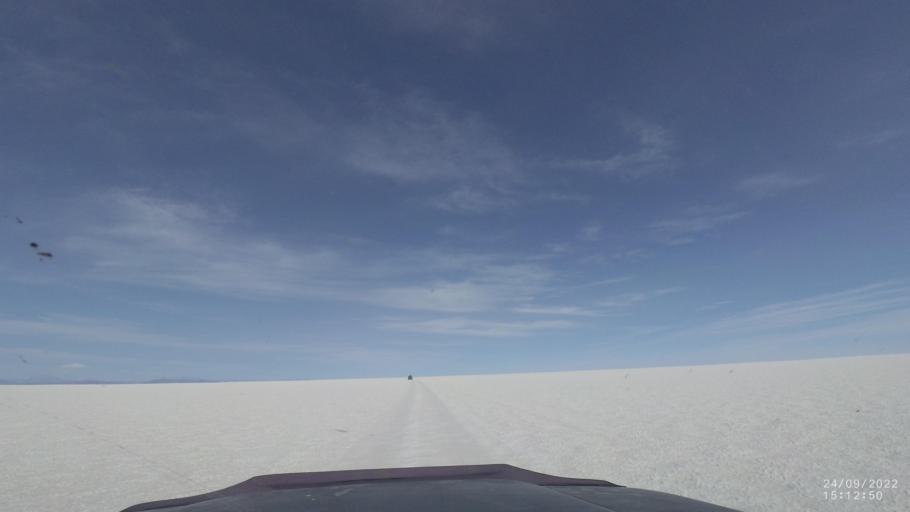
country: BO
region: Potosi
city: Colchani
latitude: -19.9508
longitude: -67.4707
